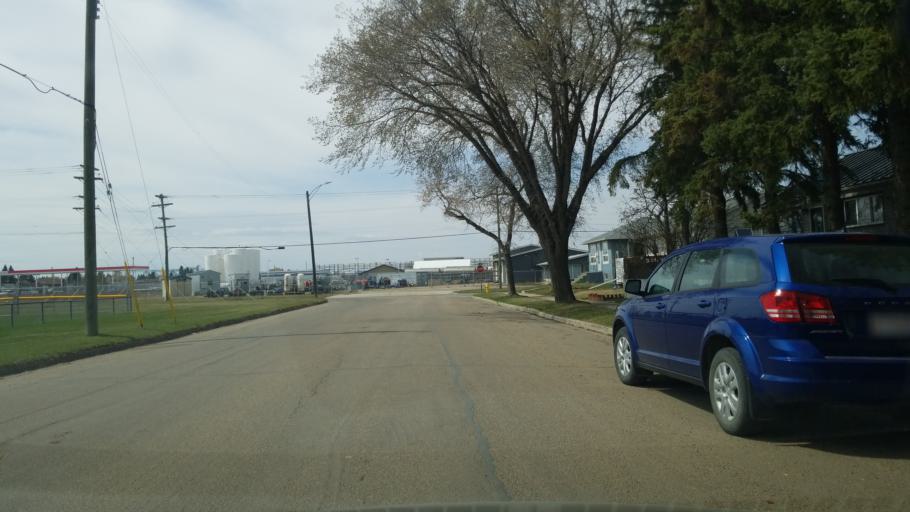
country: CA
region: Saskatchewan
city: Lloydminster
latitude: 53.2870
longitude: -110.0094
